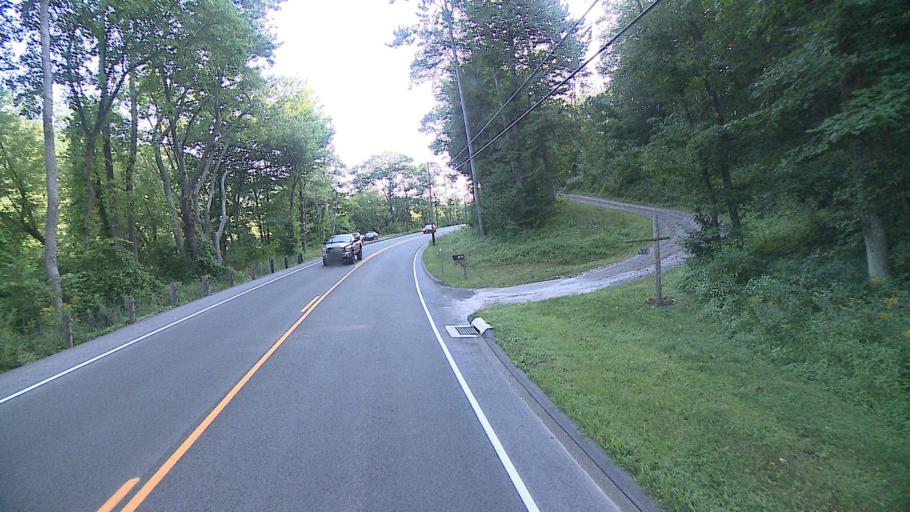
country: US
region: Connecticut
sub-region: Litchfield County
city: Kent
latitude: 41.6888
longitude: -73.5048
